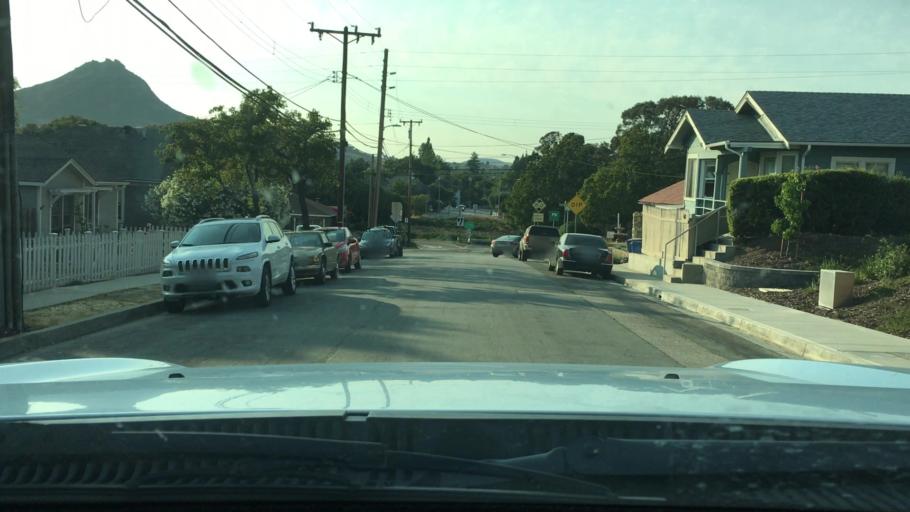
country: US
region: California
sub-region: San Luis Obispo County
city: San Luis Obispo
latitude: 35.2847
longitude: -120.6638
